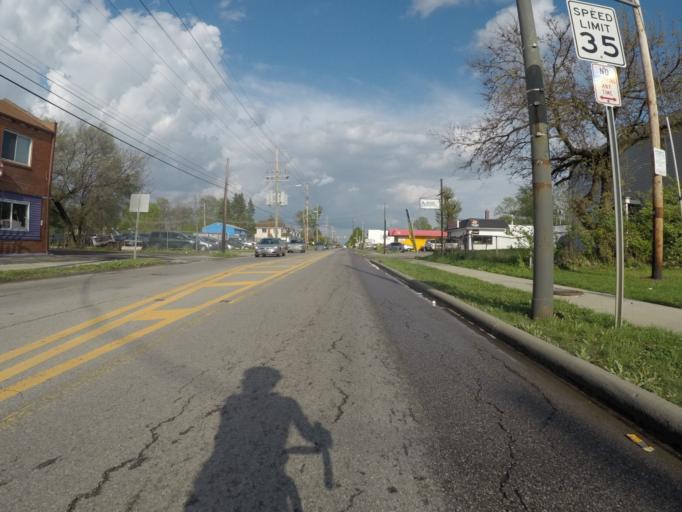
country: US
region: Ohio
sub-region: Franklin County
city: Columbus
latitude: 40.0142
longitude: -82.9808
